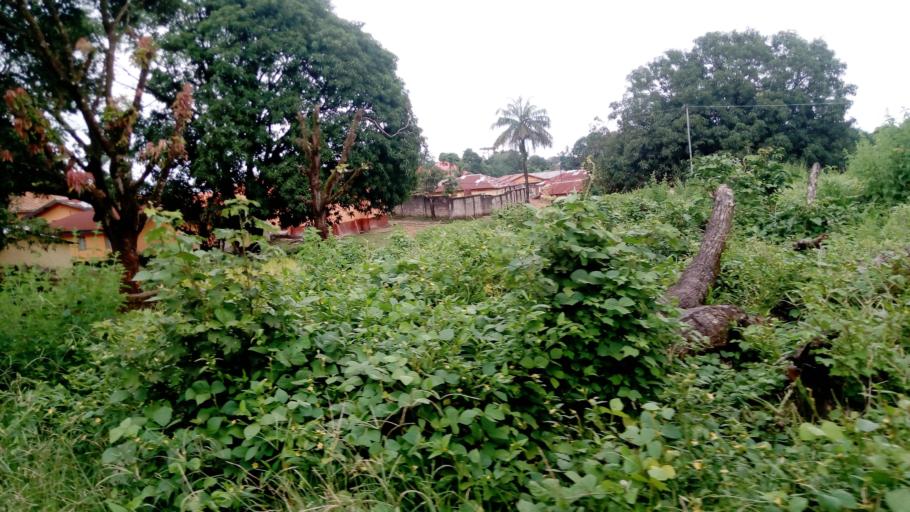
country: SL
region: Northern Province
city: Makeni
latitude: 8.8929
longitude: -12.0315
